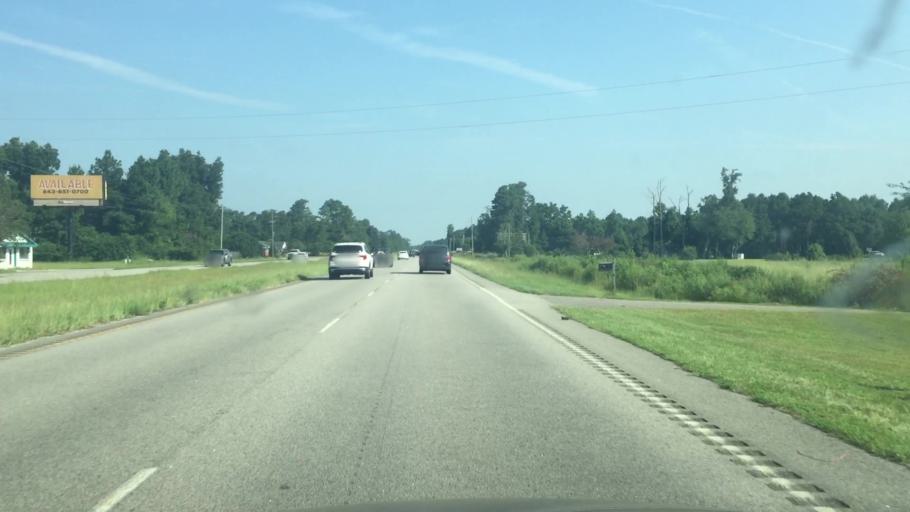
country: US
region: South Carolina
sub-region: Horry County
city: Little River
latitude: 33.9598
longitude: -78.7371
